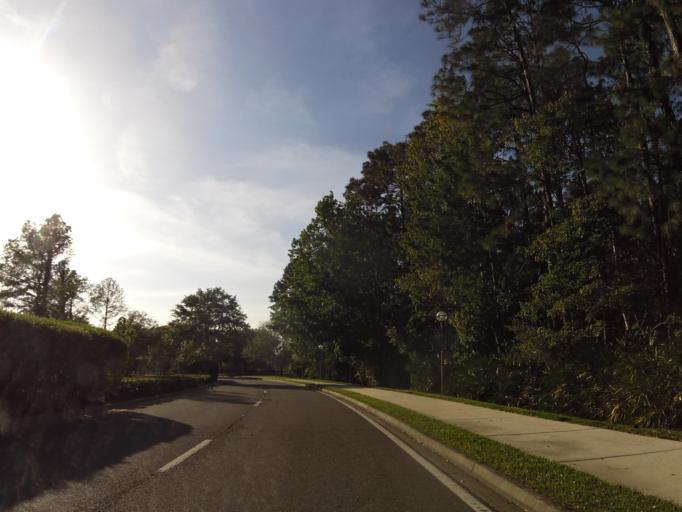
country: US
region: Florida
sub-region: Saint Johns County
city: Villano Beach
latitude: 29.9864
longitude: -81.4698
